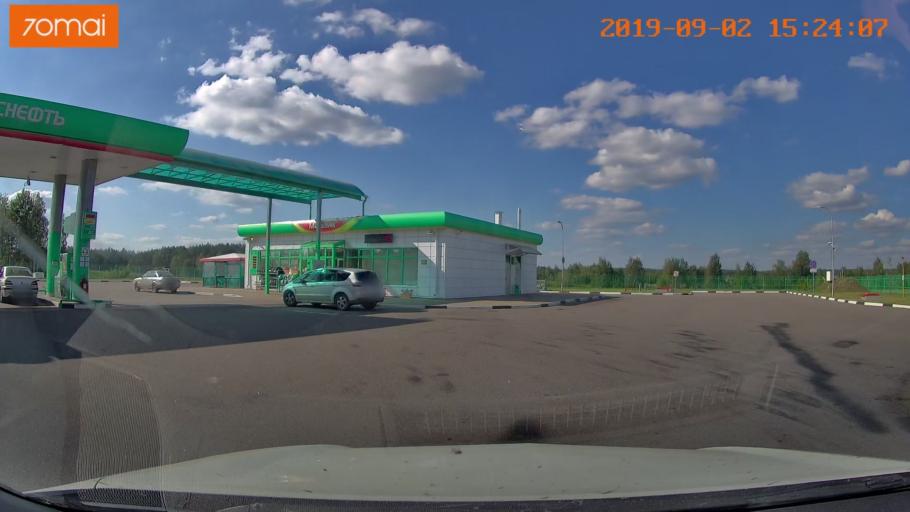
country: BY
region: Mogilev
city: Byalynichy
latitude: 53.9102
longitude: 29.4113
